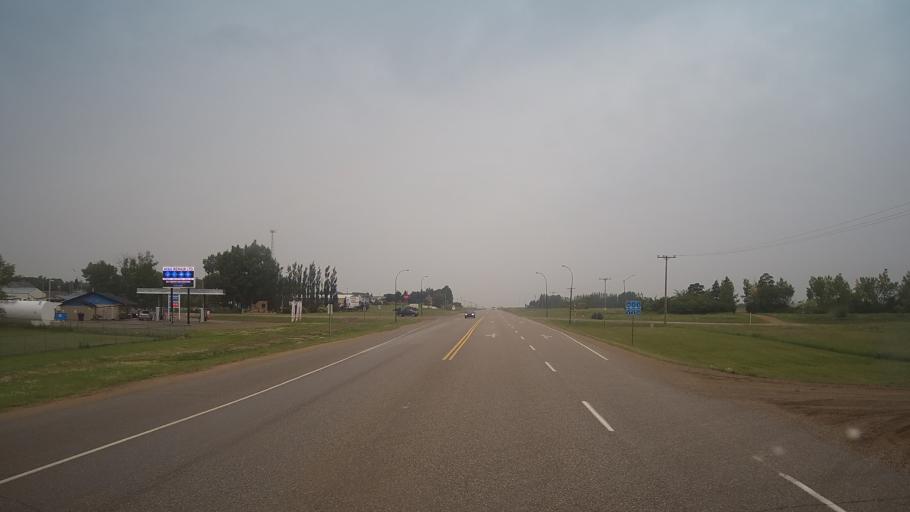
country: CA
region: Saskatchewan
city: Biggar
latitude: 52.0620
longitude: -107.9775
